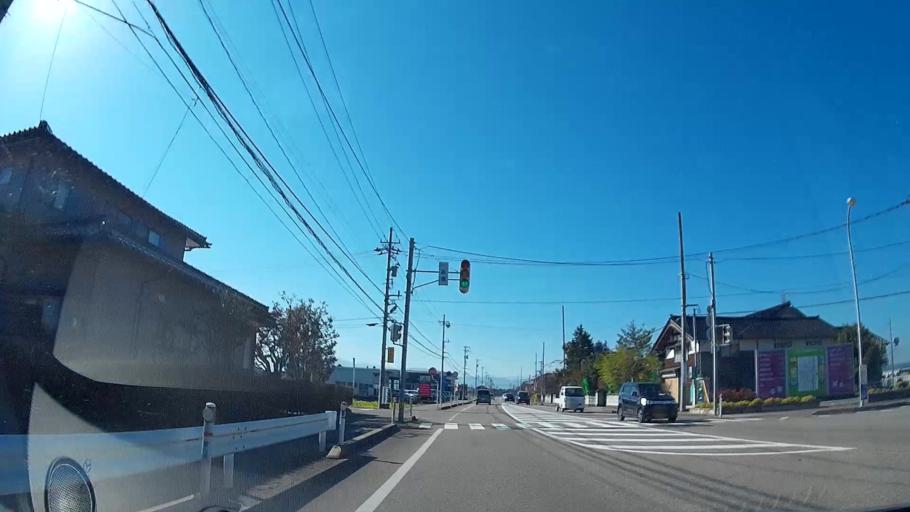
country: JP
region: Toyama
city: Nanto-shi
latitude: 36.6017
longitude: 136.9313
